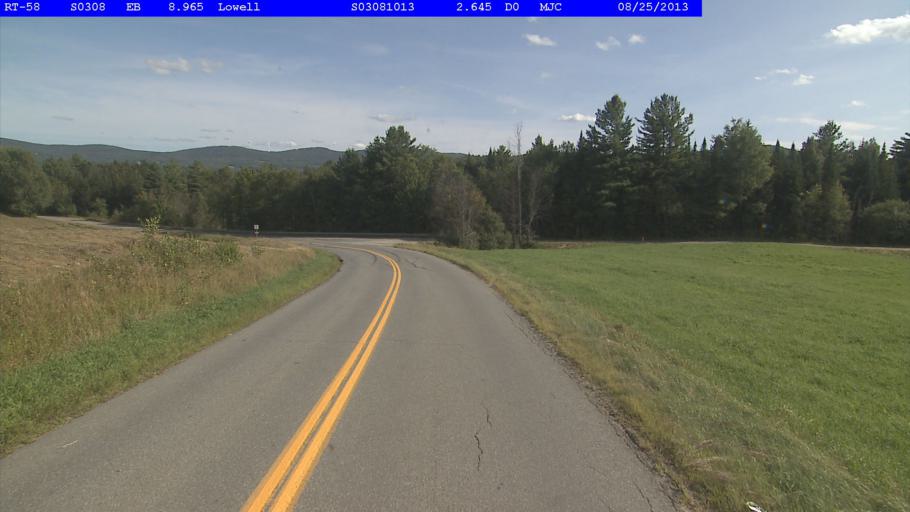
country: US
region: Vermont
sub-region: Lamoille County
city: Hyde Park
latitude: 44.8129
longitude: -72.4669
